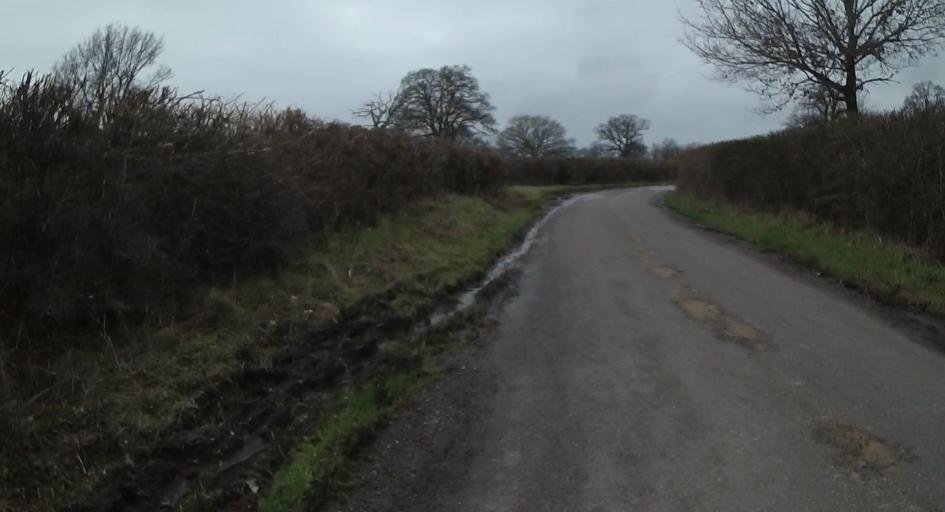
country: GB
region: England
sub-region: West Berkshire
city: Stratfield Mortimer
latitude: 51.3791
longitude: -1.0410
